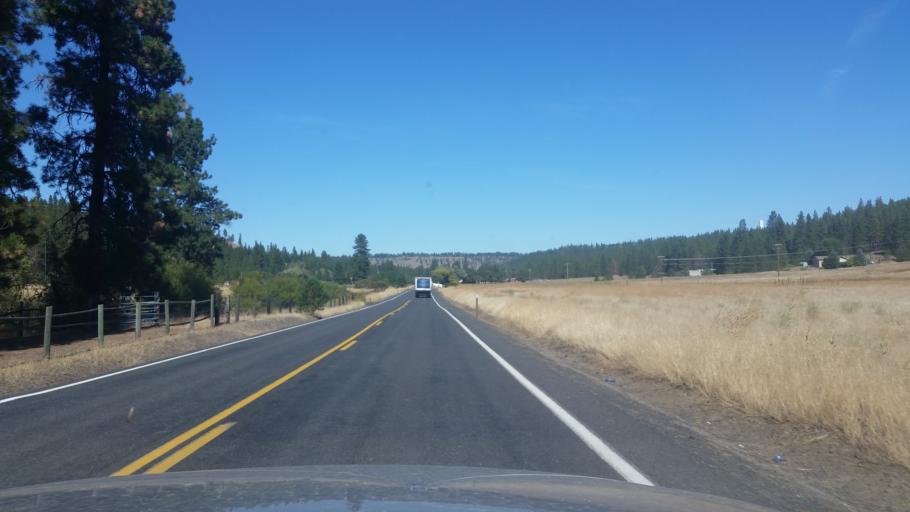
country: US
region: Washington
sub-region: Spokane County
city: Spokane
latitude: 47.5883
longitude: -117.4528
